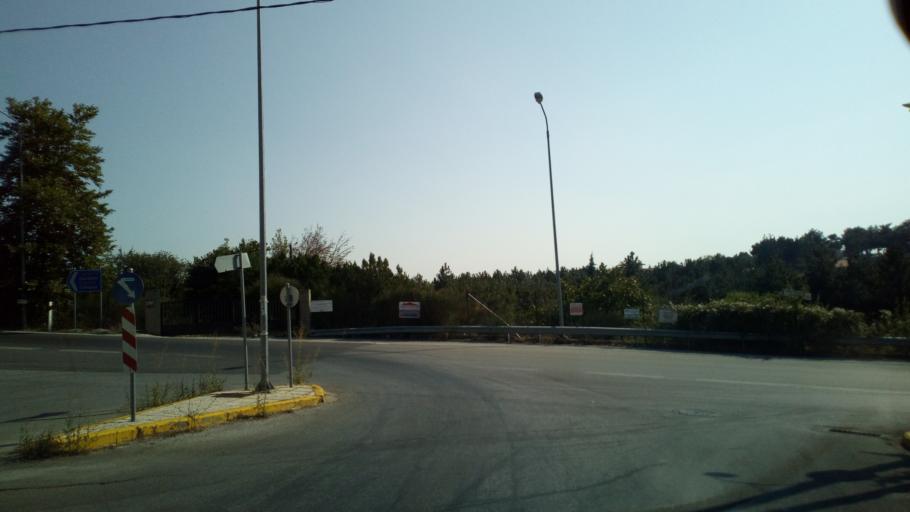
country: GR
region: Central Macedonia
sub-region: Nomos Chalkidikis
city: Polygyros
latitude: 40.3755
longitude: 23.4514
